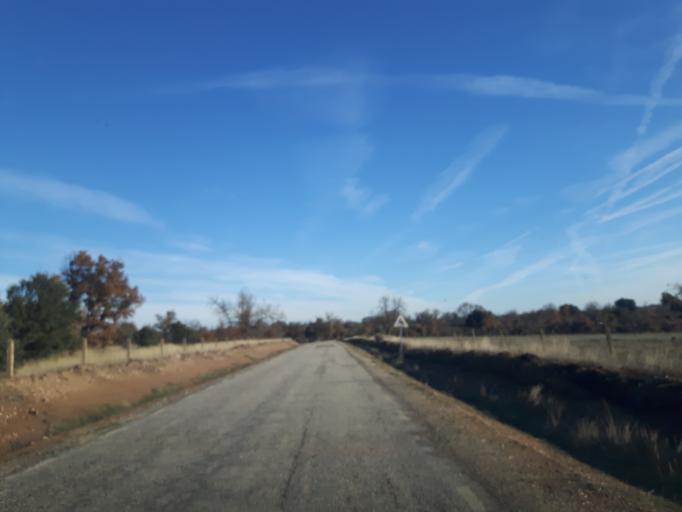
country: ES
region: Castille and Leon
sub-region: Provincia de Salamanca
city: Cerralbo
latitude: 40.9527
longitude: -6.6039
